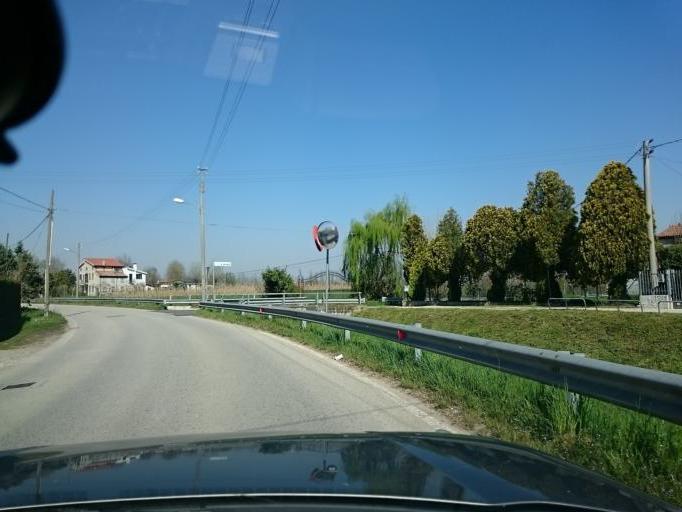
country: IT
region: Veneto
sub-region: Provincia di Padova
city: Albignasego
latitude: 45.3514
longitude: 11.9061
